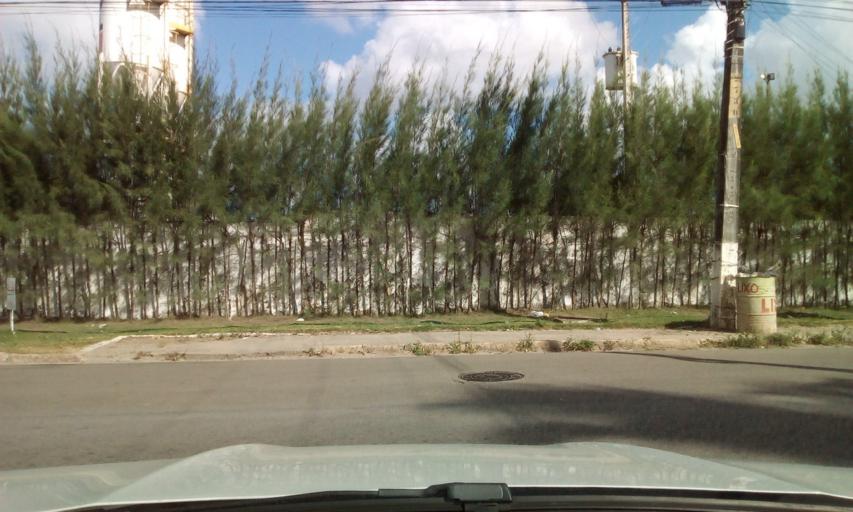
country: BR
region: Paraiba
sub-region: Bayeux
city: Bayeux
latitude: -7.1830
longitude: -34.9100
